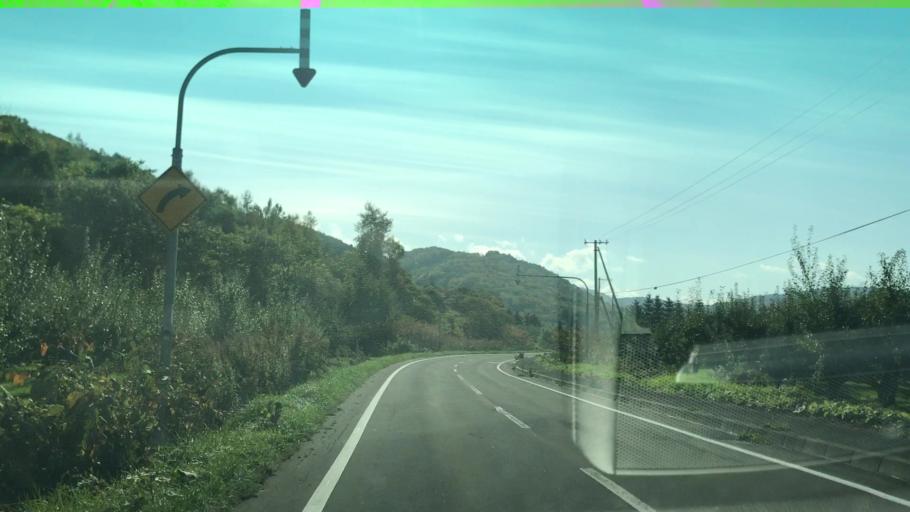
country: JP
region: Hokkaido
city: Yoichi
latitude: 43.1607
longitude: 140.8216
